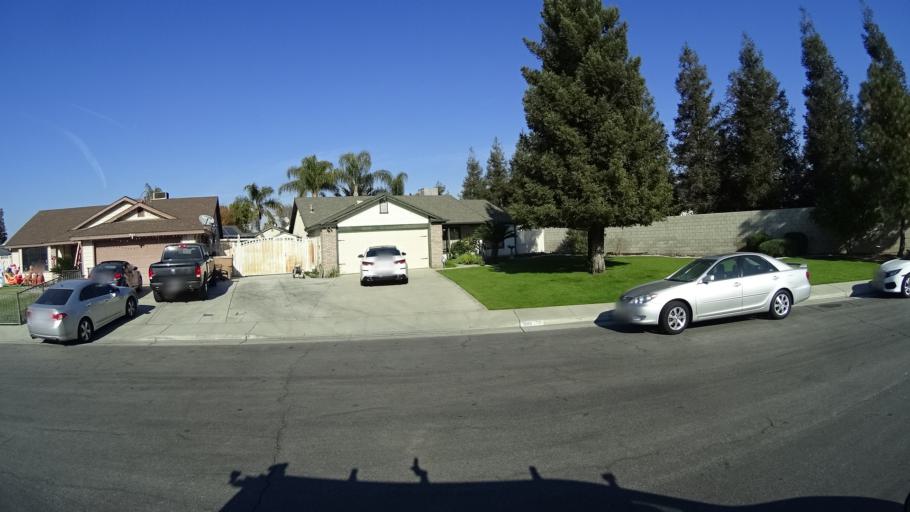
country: US
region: California
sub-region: Kern County
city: Greenfield
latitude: 35.3071
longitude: -119.0415
